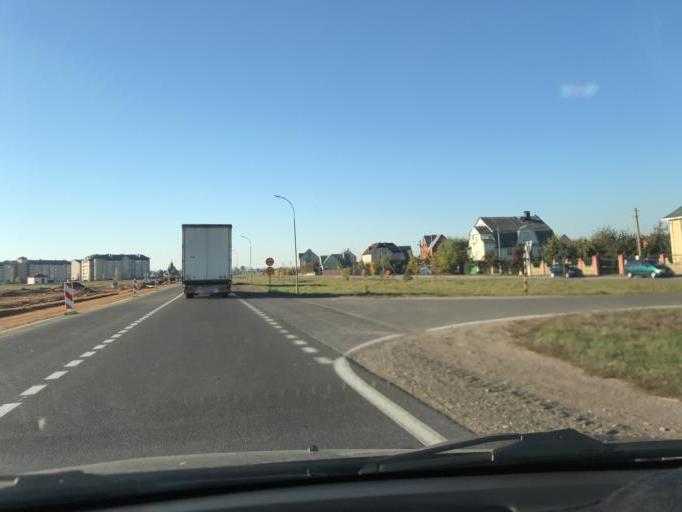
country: BY
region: Minsk
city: Slutsk
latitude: 53.0448
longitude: 27.5741
